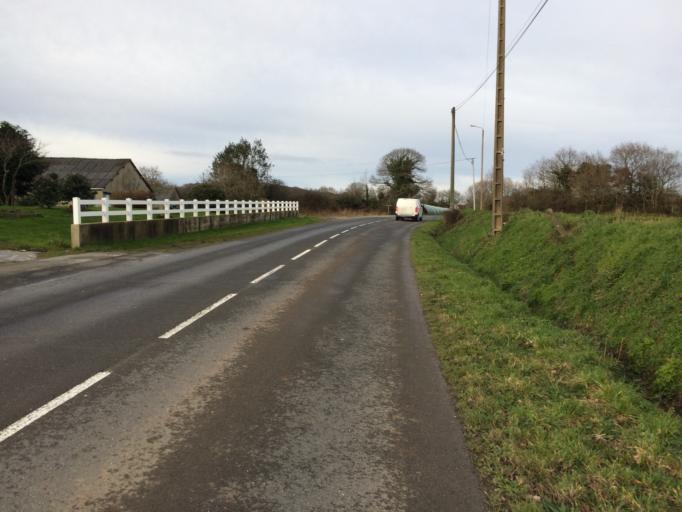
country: FR
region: Brittany
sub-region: Departement du Finistere
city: Daoulas
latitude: 48.3697
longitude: -4.2563
